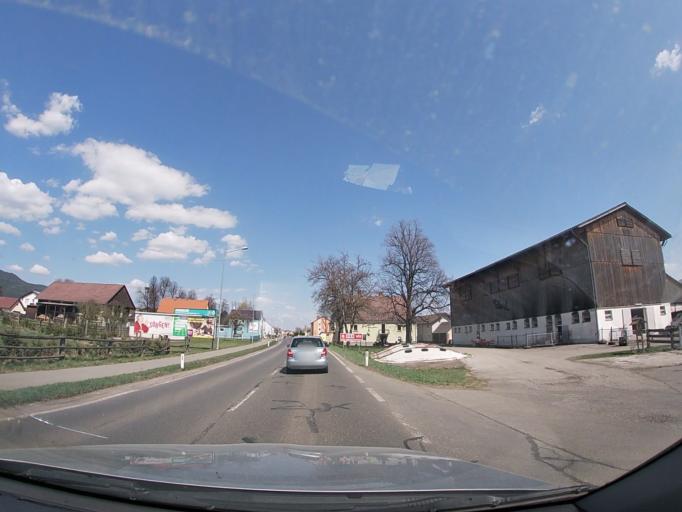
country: AT
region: Styria
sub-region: Politischer Bezirk Murtal
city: Spielberg bei Knittelfeld
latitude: 47.2049
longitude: 14.7935
